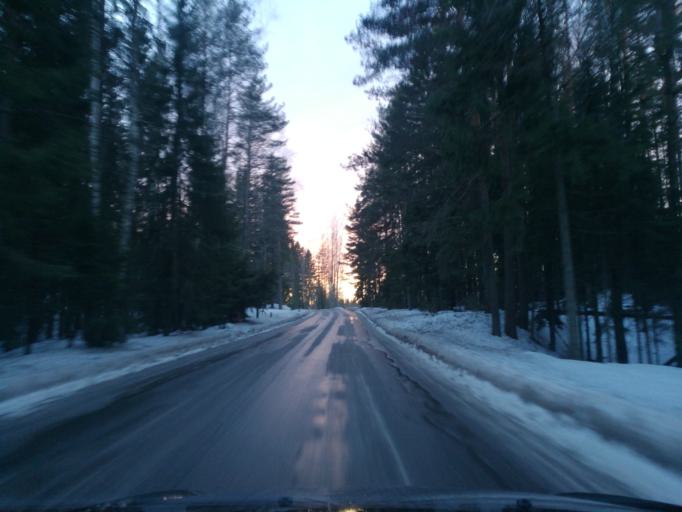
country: FI
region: Uusimaa
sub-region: Helsinki
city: Kerava
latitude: 60.3980
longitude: 25.1690
